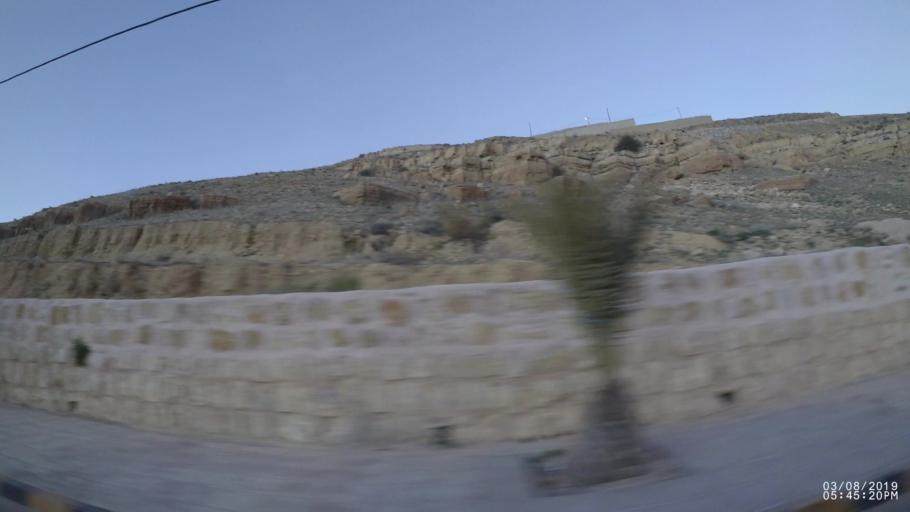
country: JO
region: Ma'an
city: Petra
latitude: 30.3134
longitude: 35.4837
